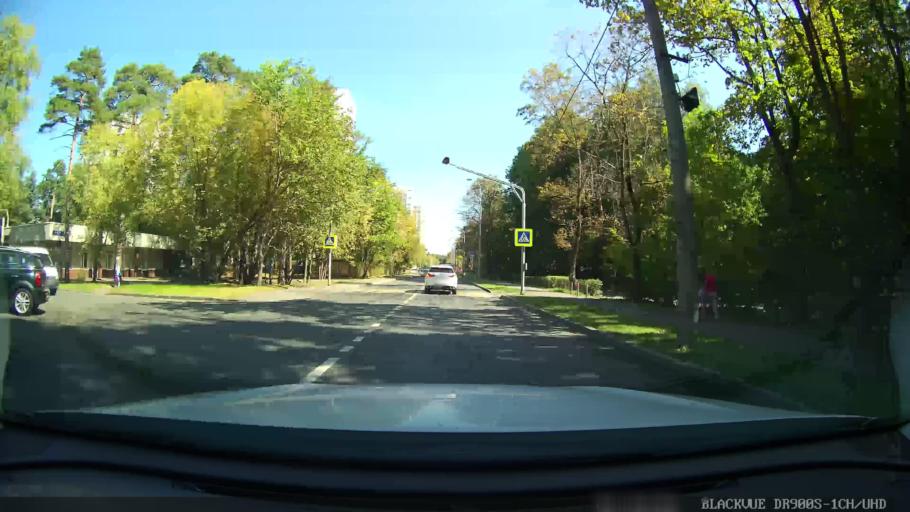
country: RU
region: Moscow
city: Pokrovskoye-Streshnevo
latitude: 55.8091
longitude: 37.4699
